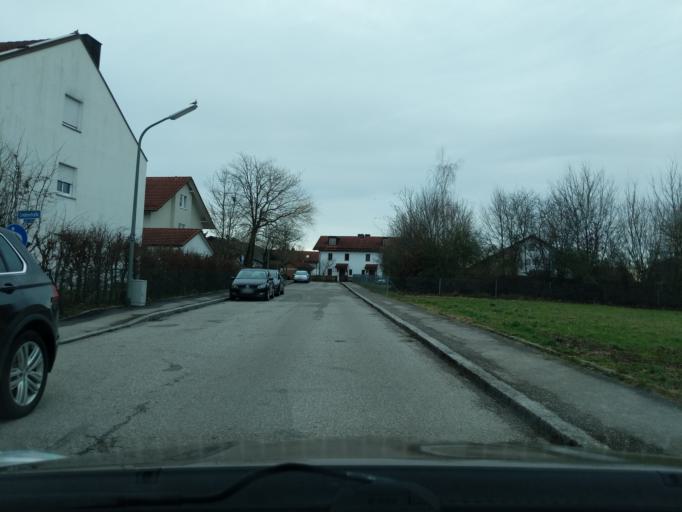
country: DE
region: Bavaria
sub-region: Upper Bavaria
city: Zorneding
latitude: 48.0844
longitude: 11.8300
